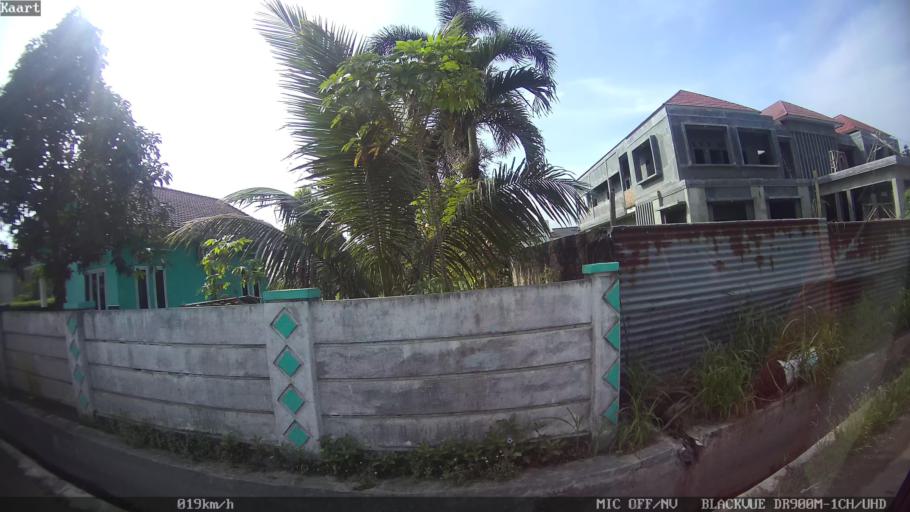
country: ID
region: Lampung
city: Kedaton
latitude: -5.3802
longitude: 105.2985
